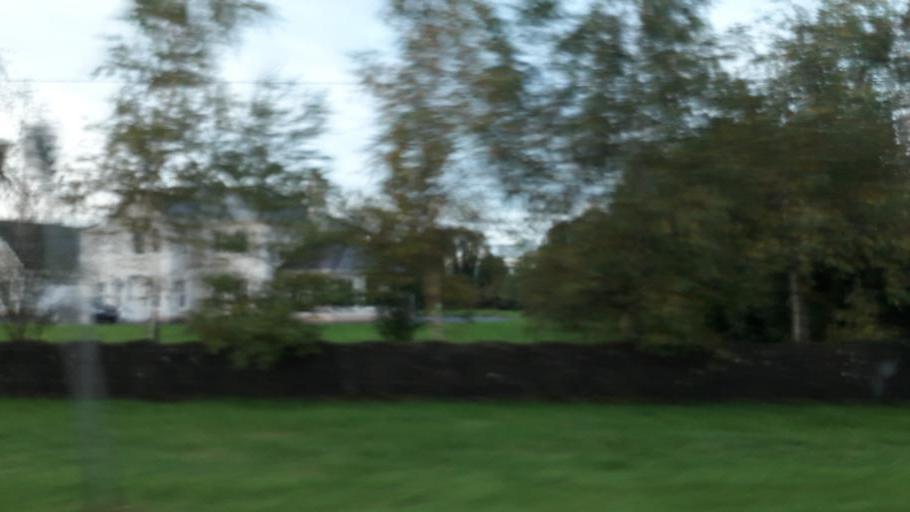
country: IE
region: Leinster
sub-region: An Longfort
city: Longford
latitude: 53.7253
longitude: -7.8385
